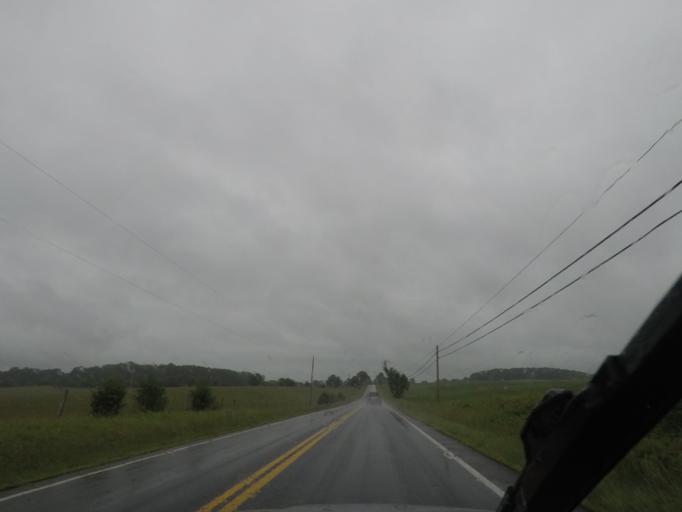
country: US
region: Virginia
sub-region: Orange County
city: Orange
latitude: 38.3256
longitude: -78.1275
